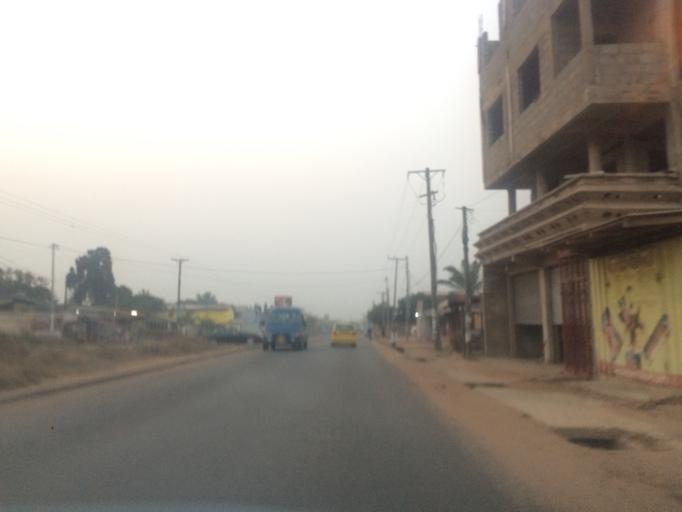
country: GH
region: Greater Accra
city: Teshi Old Town
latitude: 5.5942
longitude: -0.1009
